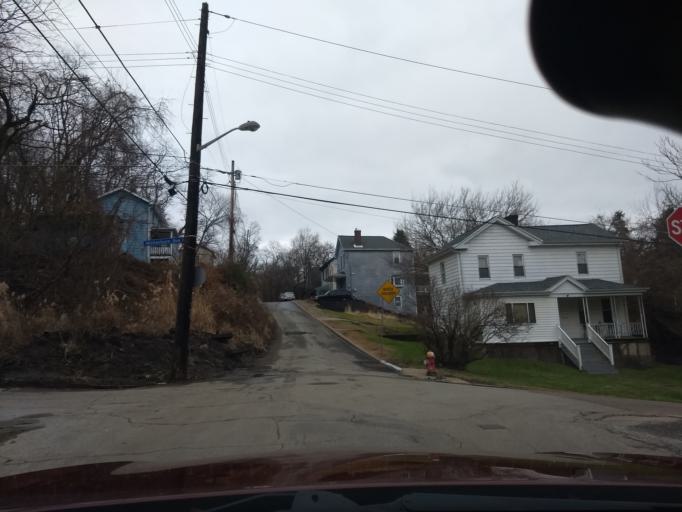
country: US
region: Pennsylvania
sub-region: Allegheny County
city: Homestead
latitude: 40.4173
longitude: -79.9402
